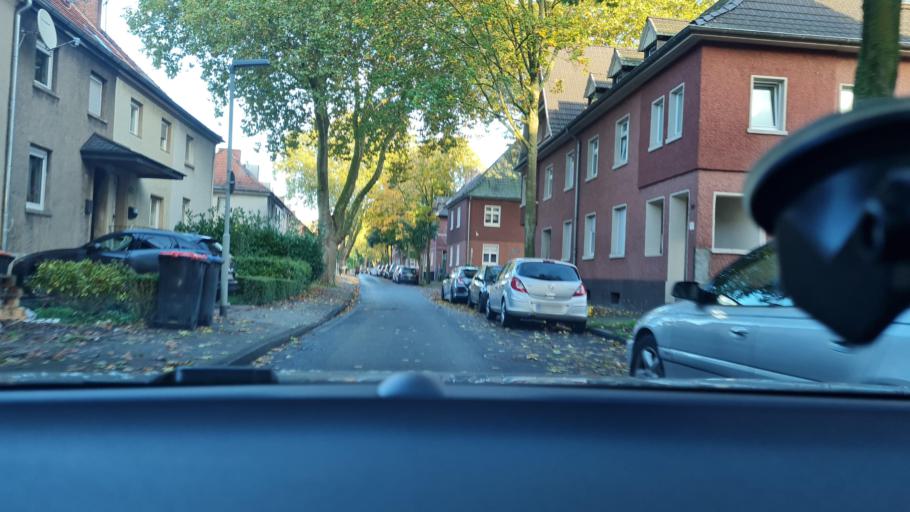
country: DE
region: North Rhine-Westphalia
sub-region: Regierungsbezirk Dusseldorf
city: Dinslaken
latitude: 51.5861
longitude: 6.7520
